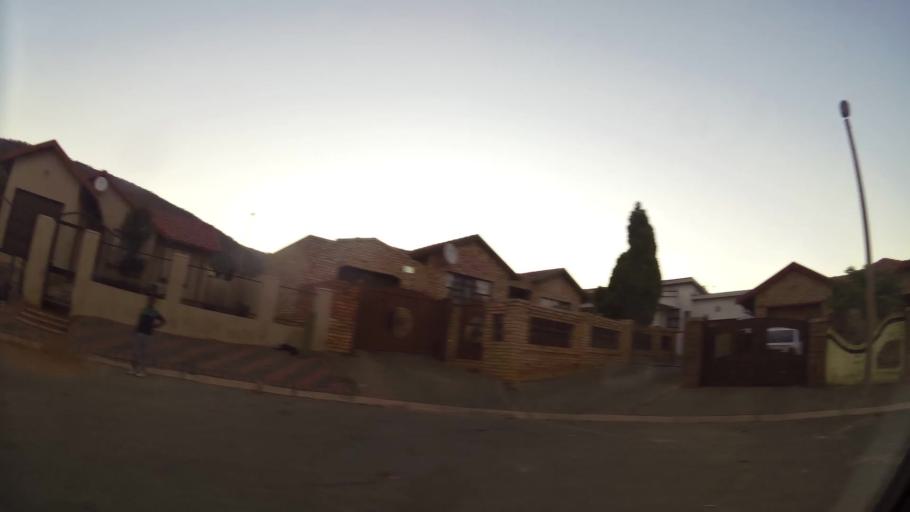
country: ZA
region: North-West
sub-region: Bojanala Platinum District Municipality
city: Rustenburg
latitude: -25.6574
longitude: 27.2026
